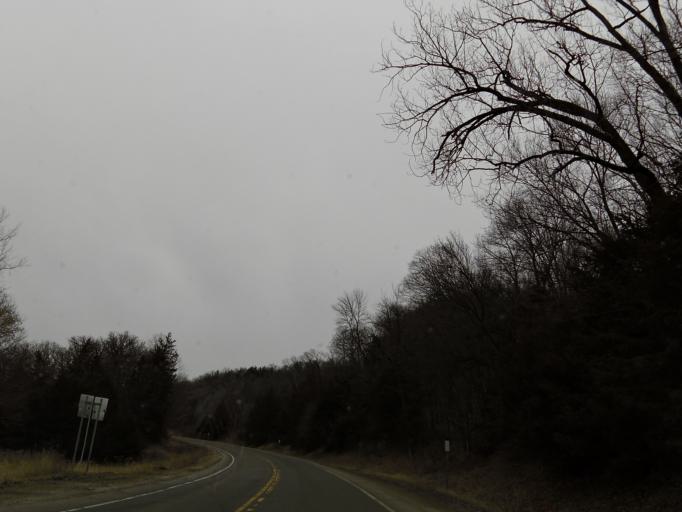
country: US
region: Minnesota
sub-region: Le Sueur County
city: Le Sueur
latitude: 44.5334
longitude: -93.8857
